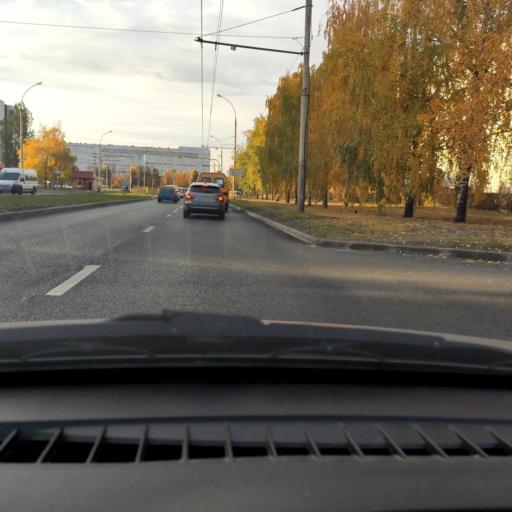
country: RU
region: Samara
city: Tol'yatti
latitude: 53.5272
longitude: 49.3269
